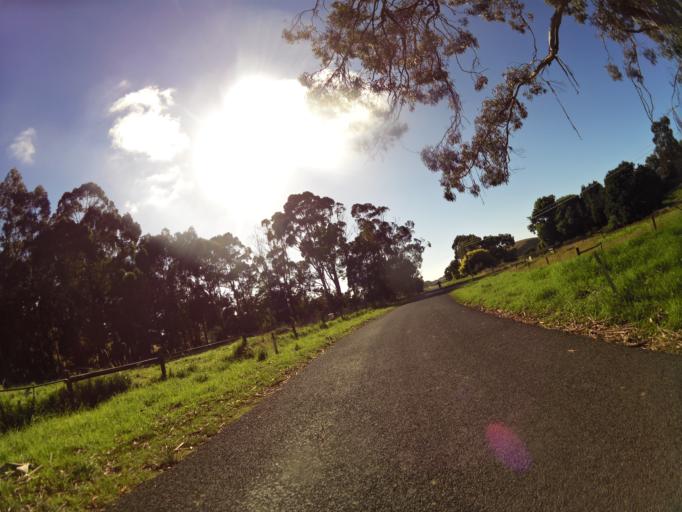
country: AU
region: Victoria
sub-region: Colac-Otway
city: Apollo Bay
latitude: -38.7655
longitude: 143.6374
